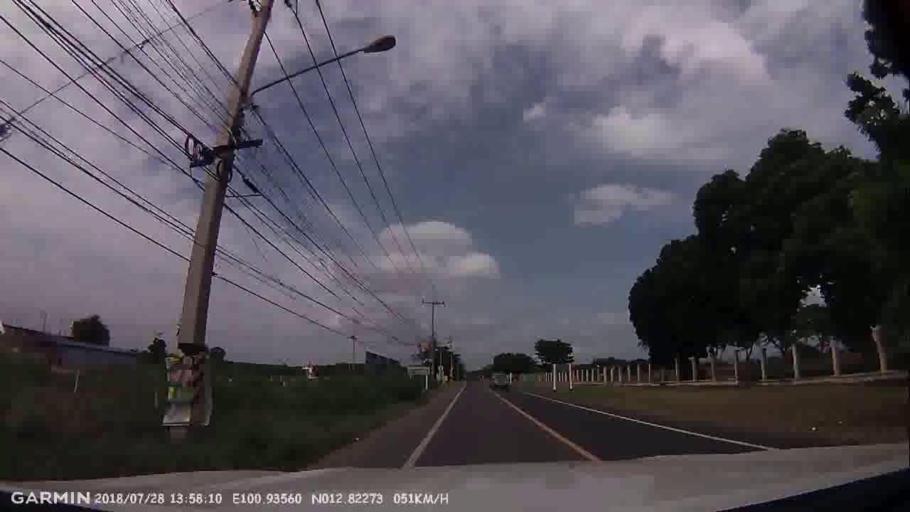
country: TH
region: Chon Buri
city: Phatthaya
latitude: 12.8227
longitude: 100.9356
